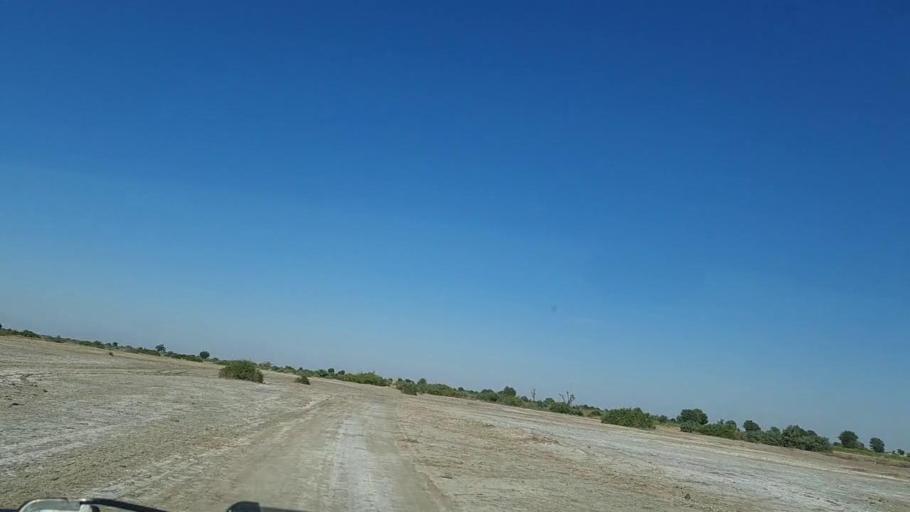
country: PK
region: Sindh
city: Pithoro
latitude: 25.5550
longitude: 69.4601
